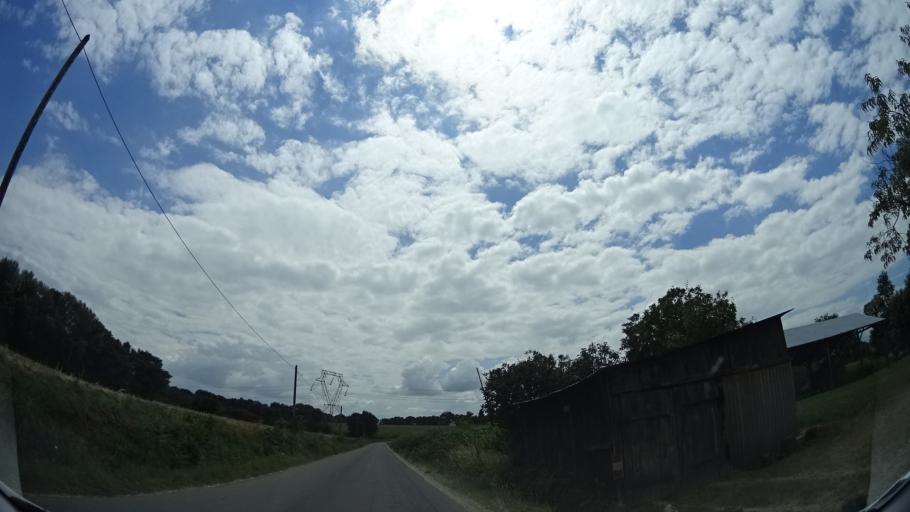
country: FR
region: Brittany
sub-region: Departement d'Ille-et-Vilaine
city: La Meziere
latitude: 48.1940
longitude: -1.7680
